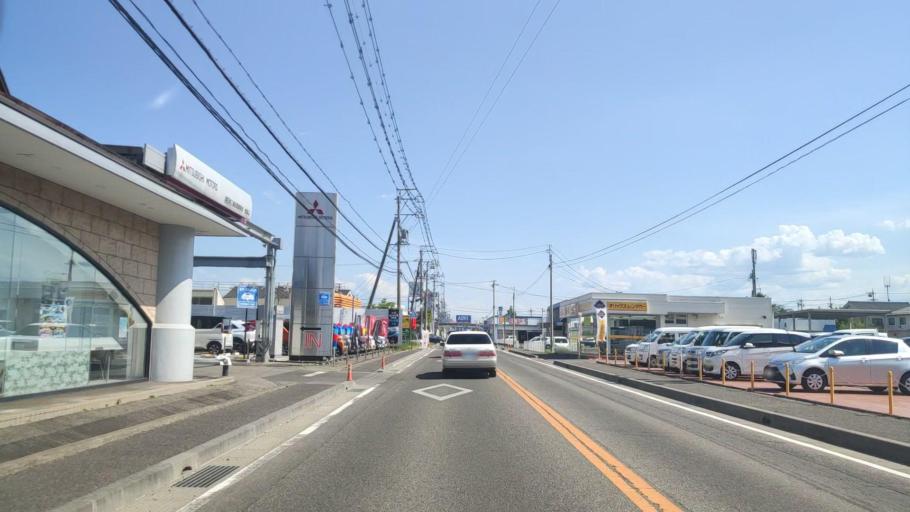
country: JP
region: Nagano
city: Hotaka
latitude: 36.3358
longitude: 137.8897
